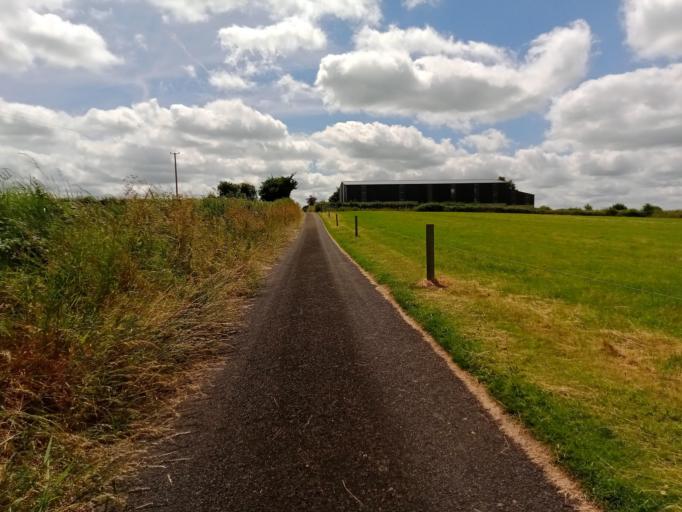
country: IE
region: Leinster
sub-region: Kilkenny
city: Callan
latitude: 52.5483
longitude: -7.4184
